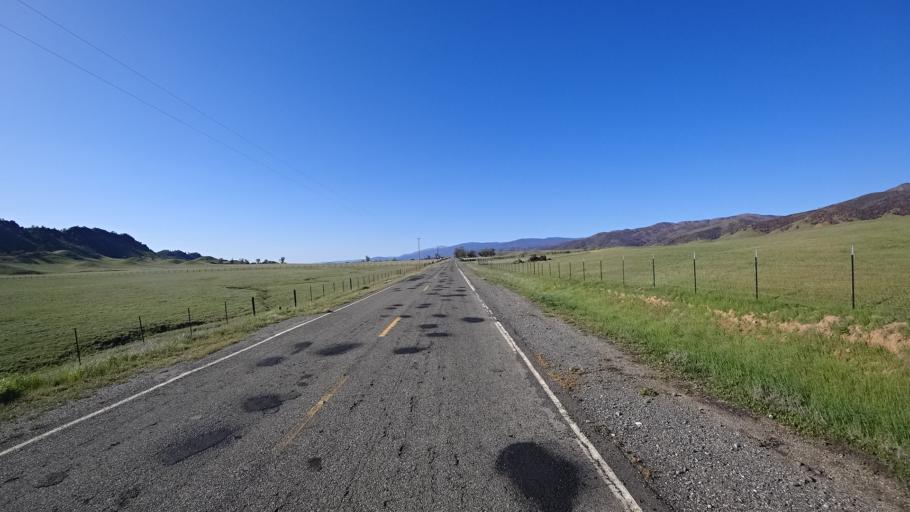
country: US
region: California
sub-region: Tehama County
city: Rancho Tehama Reserve
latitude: 39.7380
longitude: -122.5459
